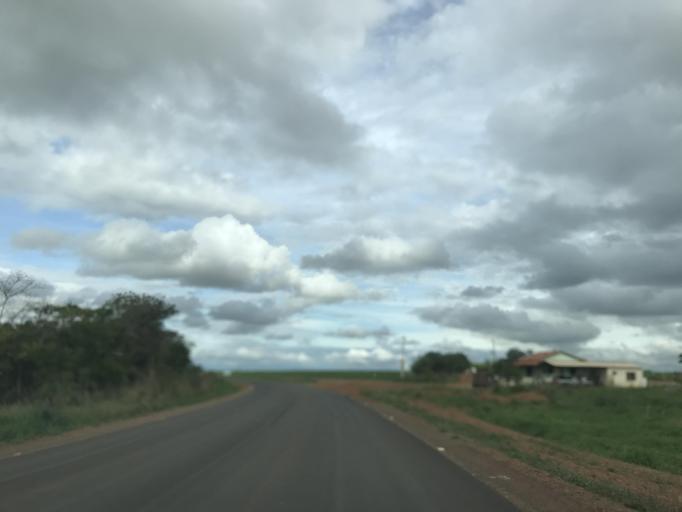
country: BR
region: Goias
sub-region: Vianopolis
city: Vianopolis
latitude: -16.9680
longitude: -48.6027
